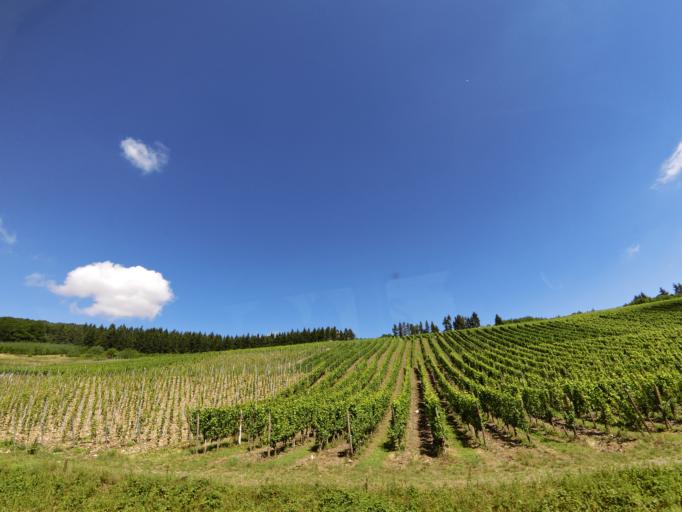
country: DE
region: Rheinland-Pfalz
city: Osann-Monzel
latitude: 49.9195
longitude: 6.9209
